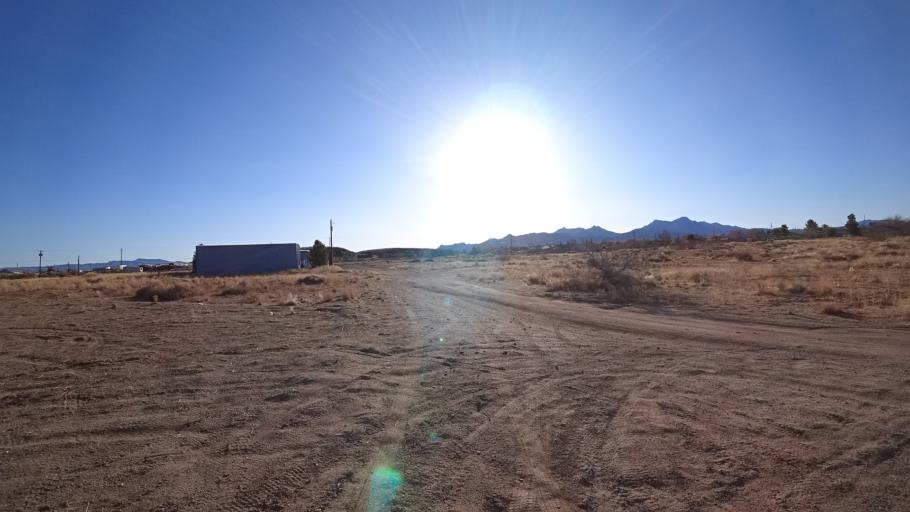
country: US
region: Arizona
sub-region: Mohave County
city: Kingman
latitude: 35.2084
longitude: -114.0152
